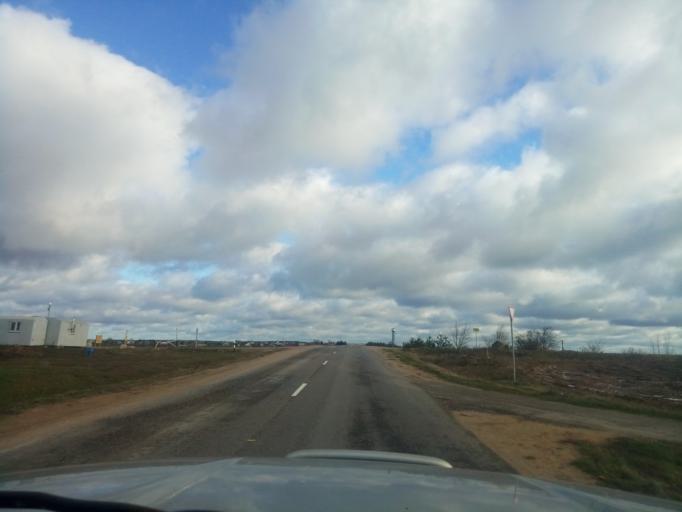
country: BY
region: Minsk
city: Kapyl'
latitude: 53.1486
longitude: 27.0612
